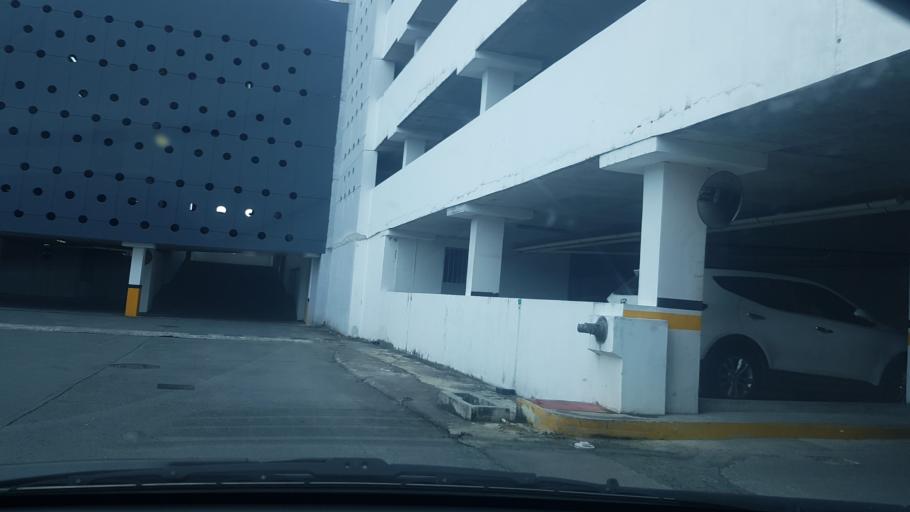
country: PA
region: Panama
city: Panama
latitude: 9.0187
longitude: -79.5164
